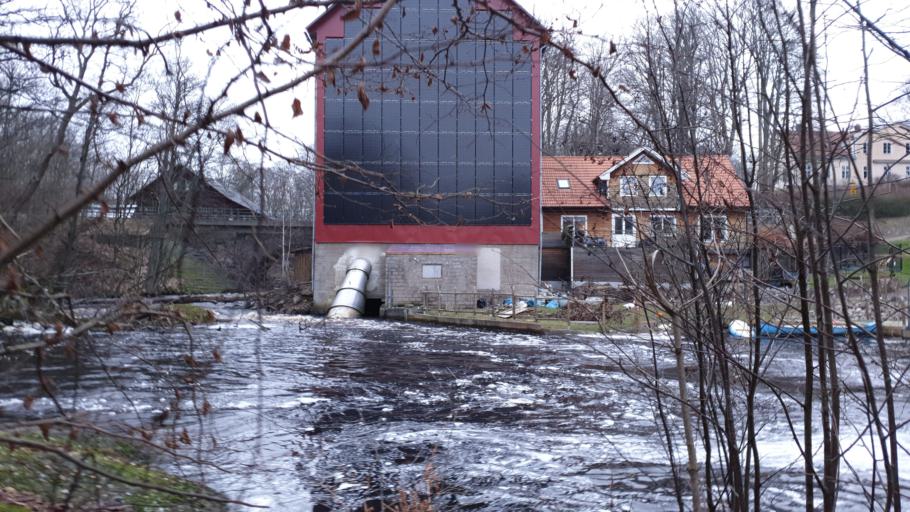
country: SE
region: Blekinge
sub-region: Karlskrona Kommun
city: Rodeby
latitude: 56.2163
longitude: 15.6736
